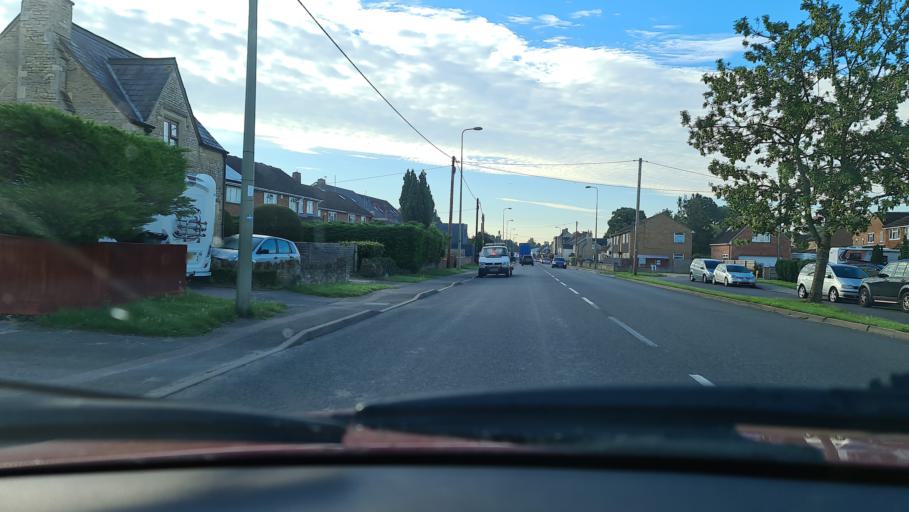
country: GB
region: England
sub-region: Oxfordshire
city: Kidlington
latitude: 51.8258
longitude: -1.2940
